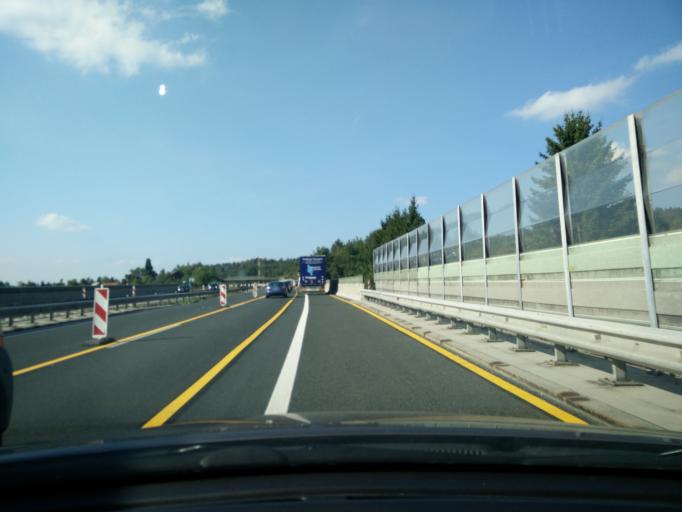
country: SI
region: Cerknica
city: Rakek
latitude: 45.8359
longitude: 14.2951
